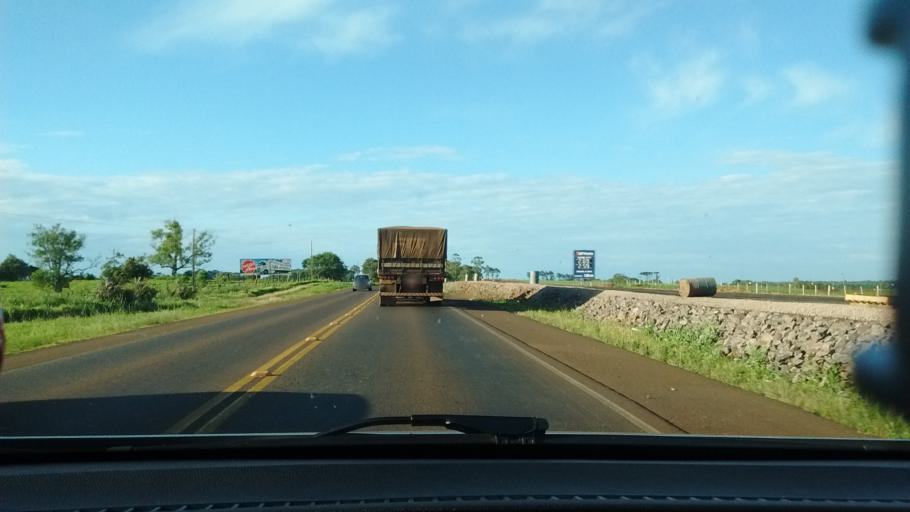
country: BR
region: Parana
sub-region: Cascavel
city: Cascavel
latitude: -25.1671
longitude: -53.5997
